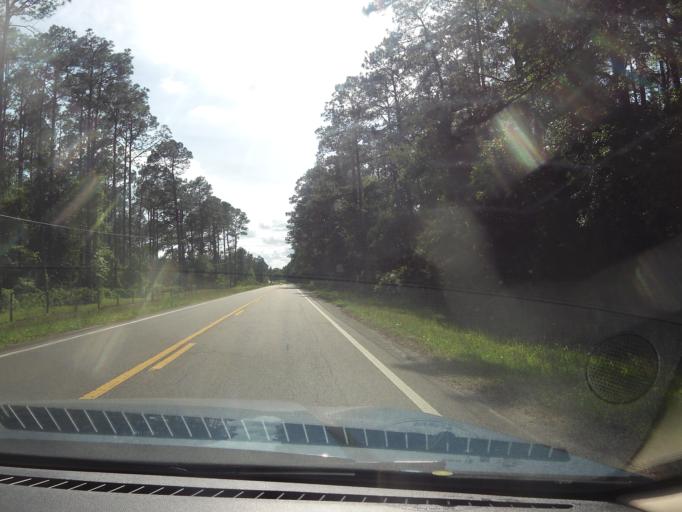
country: US
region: Florida
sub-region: Nassau County
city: Callahan
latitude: 30.5617
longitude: -81.8466
